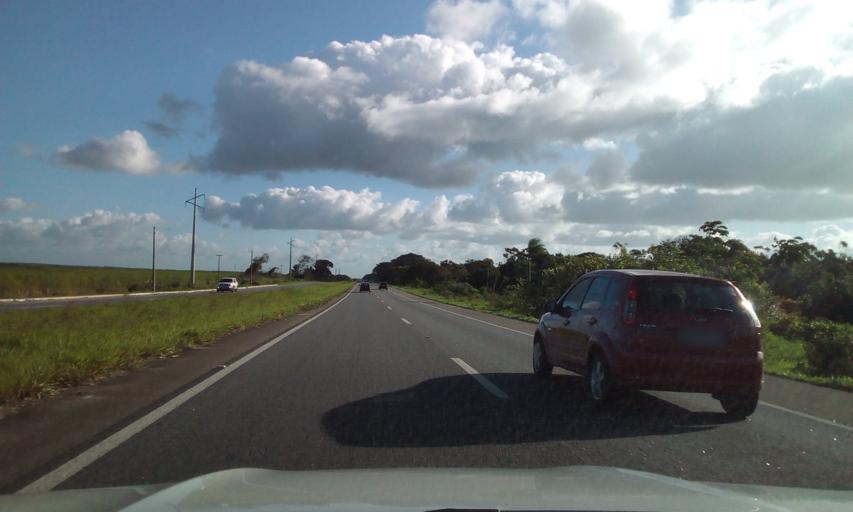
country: BR
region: Paraiba
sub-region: Cruz Do Espirito Santo
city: Cruz do Espirito Santo
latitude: -7.1679
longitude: -35.0312
